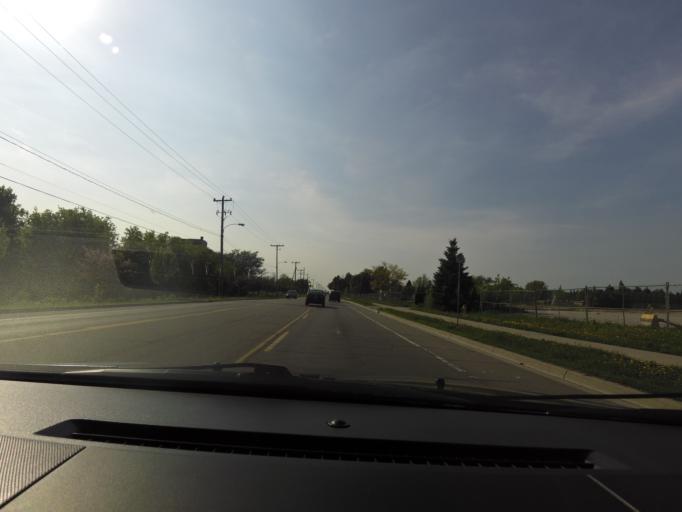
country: CA
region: Ontario
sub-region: Wellington County
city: Guelph
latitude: 43.5449
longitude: -80.2683
